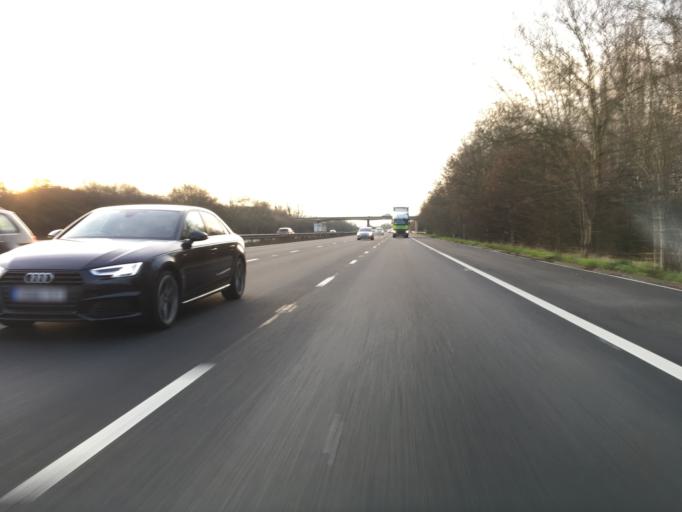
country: GB
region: England
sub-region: Gloucestershire
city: Uckington
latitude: 51.9524
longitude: -2.1270
